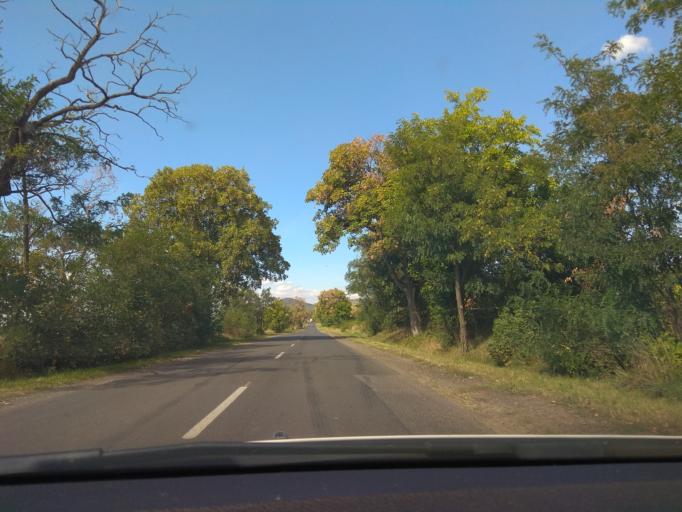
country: HU
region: Borsod-Abauj-Zemplen
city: Tallya
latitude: 48.2197
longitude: 21.2420
